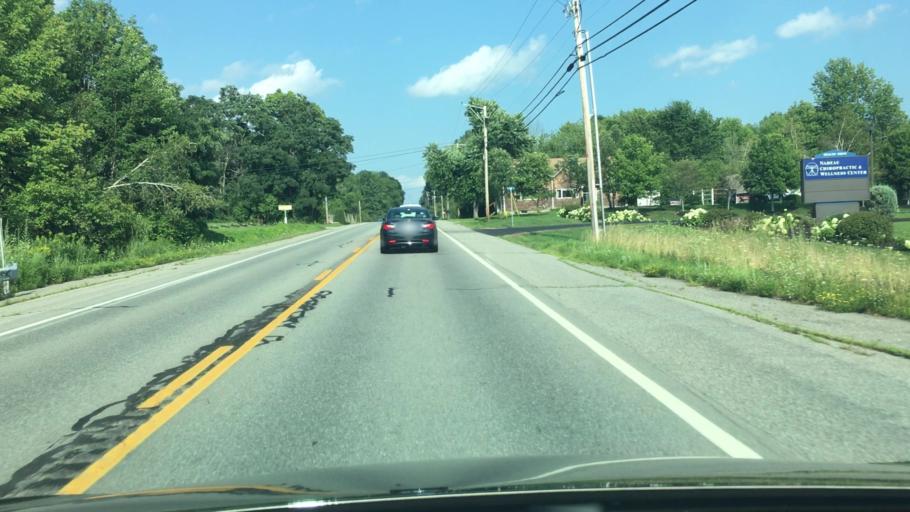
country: US
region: Maine
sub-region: Kennebec County
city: Augusta
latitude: 44.3322
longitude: -69.7163
